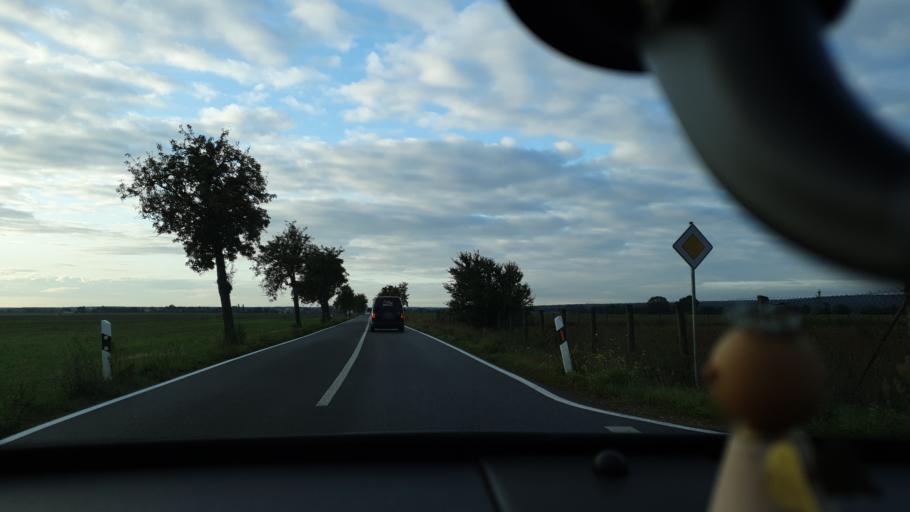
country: DE
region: Saxony
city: Schildau
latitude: 51.4766
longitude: 12.9246
